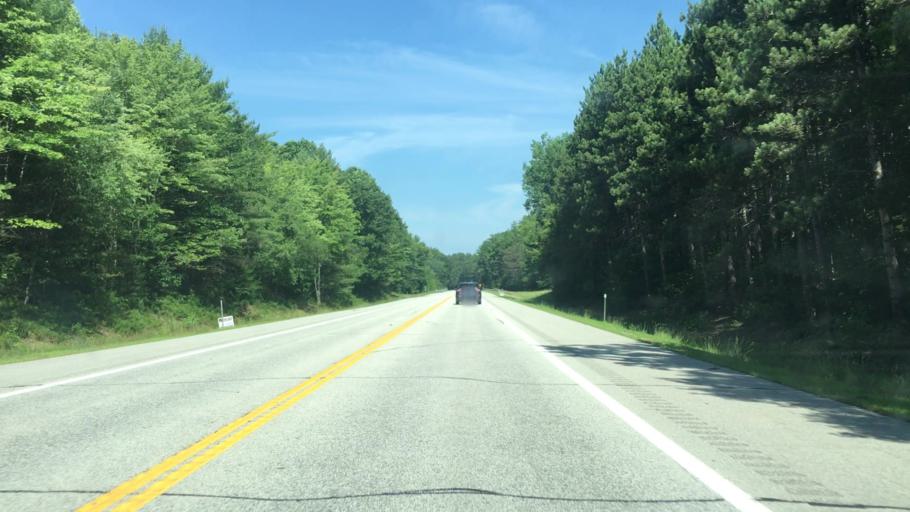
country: US
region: New Hampshire
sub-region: Merrimack County
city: Henniker
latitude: 43.1869
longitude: -71.8052
